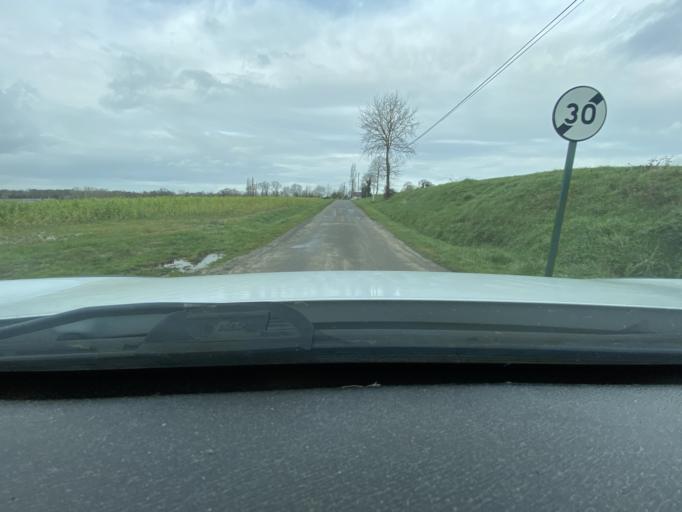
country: FR
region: Brittany
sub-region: Departement d'Ille-et-Vilaine
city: Melesse
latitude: 48.2202
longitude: -1.7081
